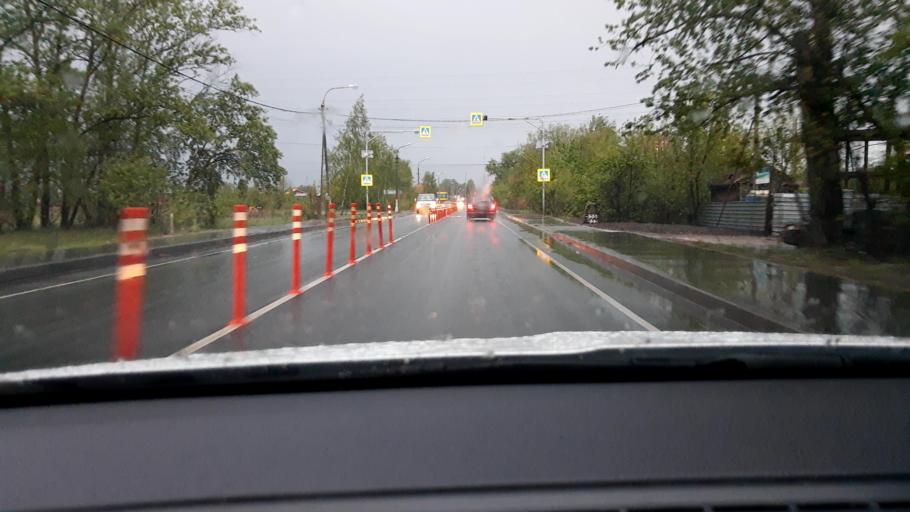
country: RU
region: Moskovskaya
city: Zagoryanskiy
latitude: 55.9285
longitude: 37.9459
